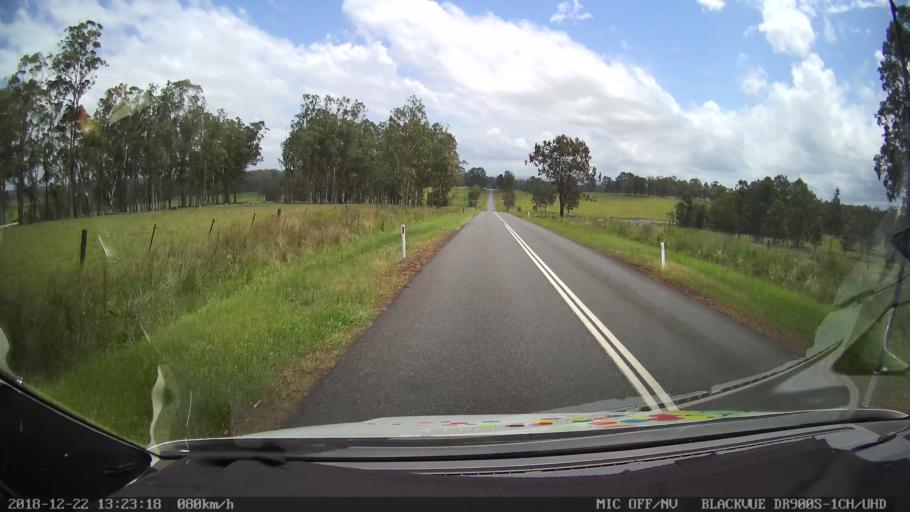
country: AU
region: New South Wales
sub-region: Clarence Valley
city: Coutts Crossing
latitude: -29.7964
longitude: 152.9082
